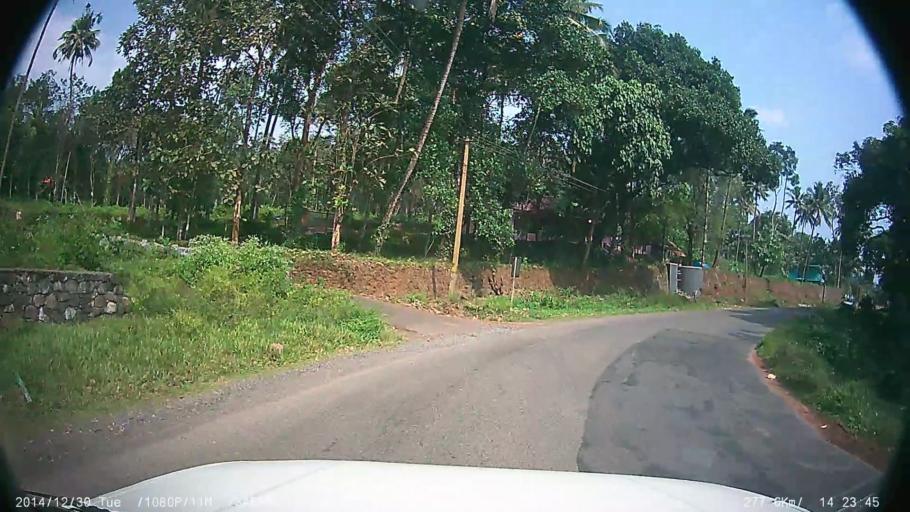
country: IN
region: Kerala
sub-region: Kottayam
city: Palackattumala
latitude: 9.8158
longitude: 76.5821
